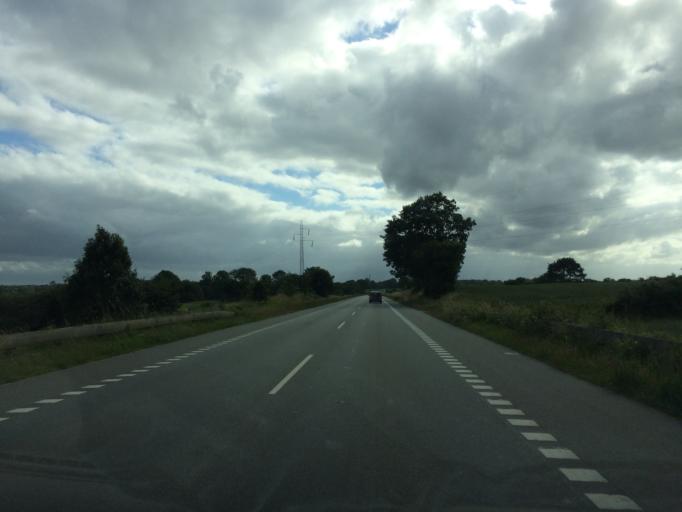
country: DK
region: South Denmark
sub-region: Sonderborg Kommune
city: Augustenborg
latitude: 54.9570
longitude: 9.9086
